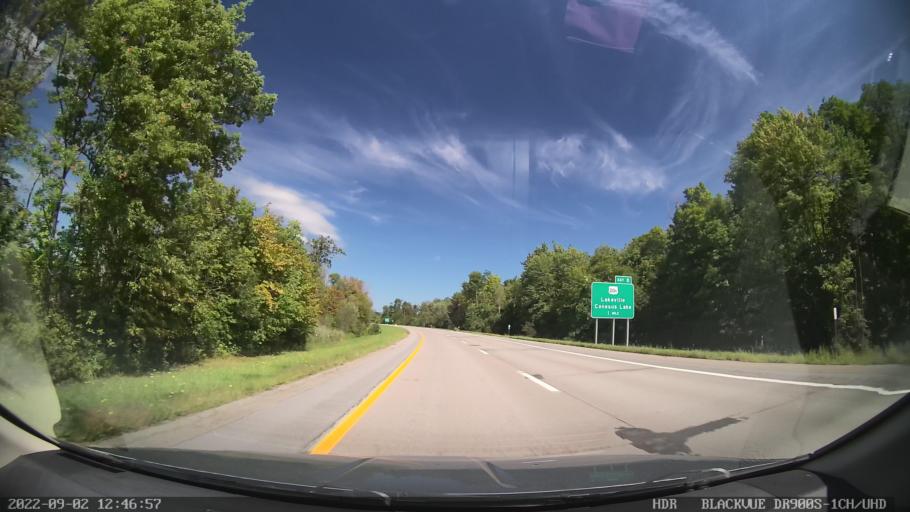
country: US
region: New York
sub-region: Livingston County
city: Livonia
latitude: 42.8070
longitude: -77.7389
